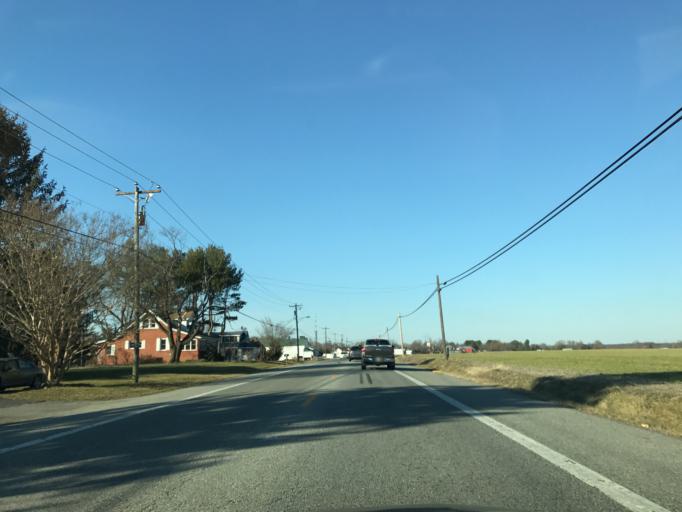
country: US
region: Maryland
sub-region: Caroline County
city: Greensboro
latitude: 39.0279
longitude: -75.7872
